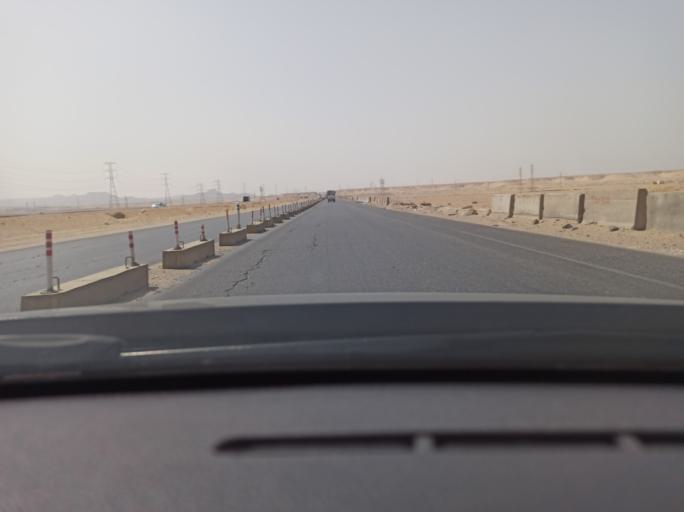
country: EG
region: Muhafazat Bani Suwayf
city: Bush
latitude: 29.1678
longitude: 31.2404
